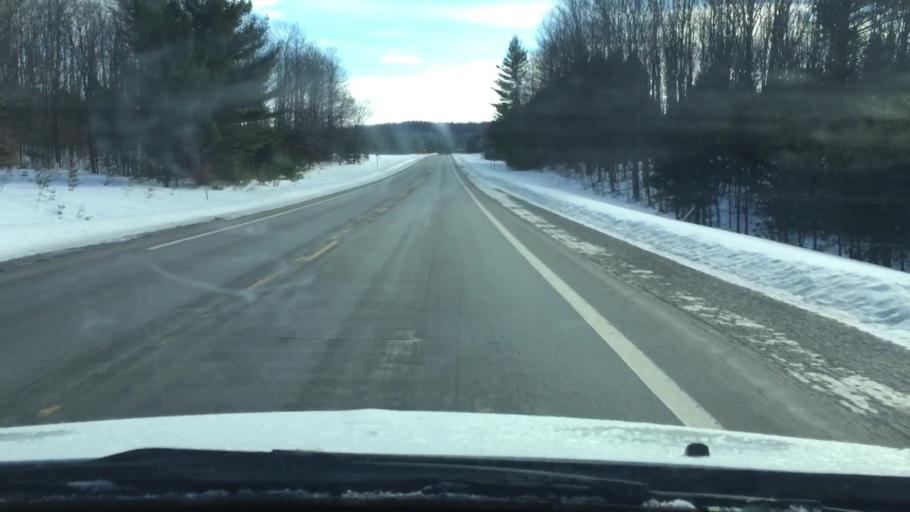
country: US
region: Michigan
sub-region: Antrim County
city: Mancelona
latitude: 44.9658
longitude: -85.0531
